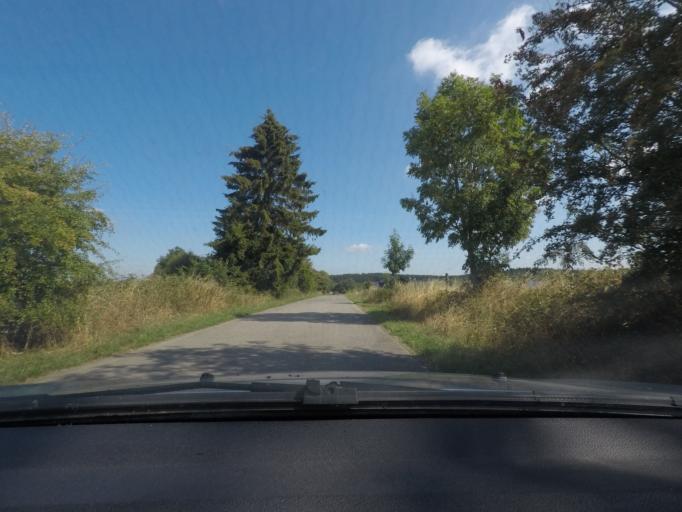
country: BE
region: Wallonia
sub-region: Province du Luxembourg
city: Fauvillers
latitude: 49.7952
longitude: 5.6291
